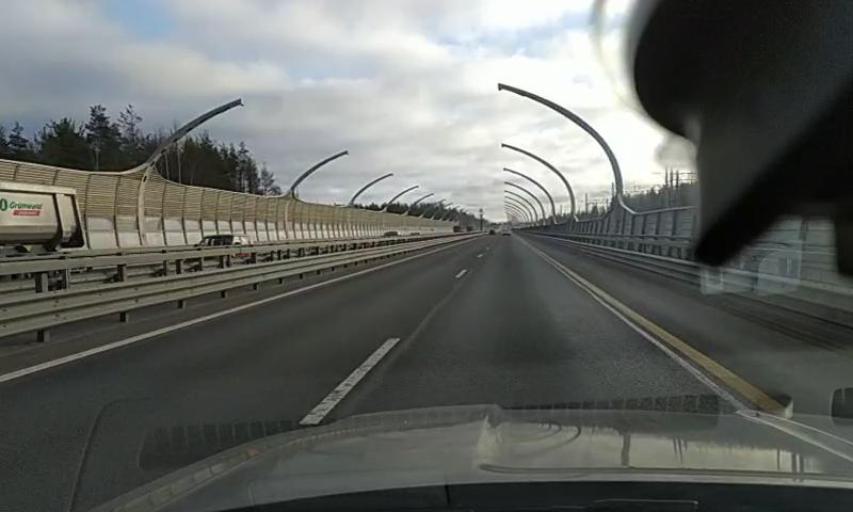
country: RU
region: St.-Petersburg
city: Beloostrov
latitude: 60.1435
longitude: 30.0217
